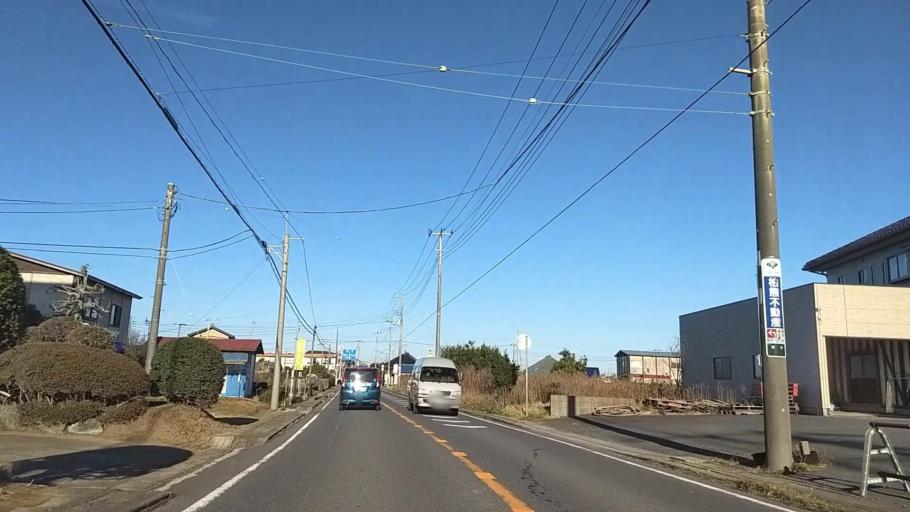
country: JP
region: Chiba
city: Yokaichiba
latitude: 35.6530
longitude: 140.5893
